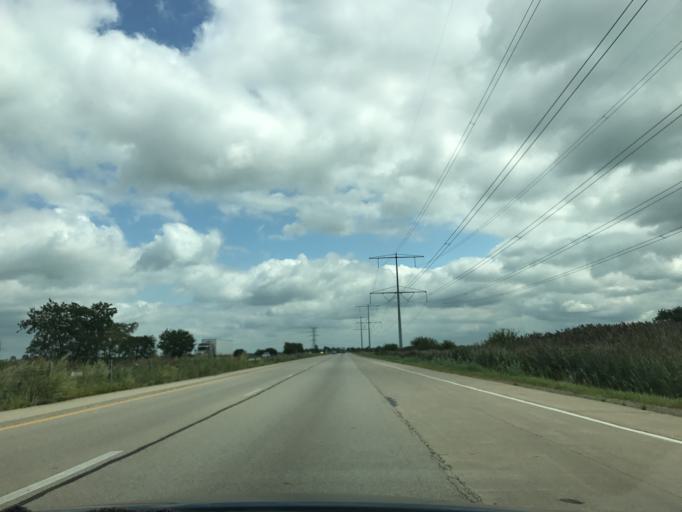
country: US
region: Illinois
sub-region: LaSalle County
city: Seneca
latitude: 41.3771
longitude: -88.5498
